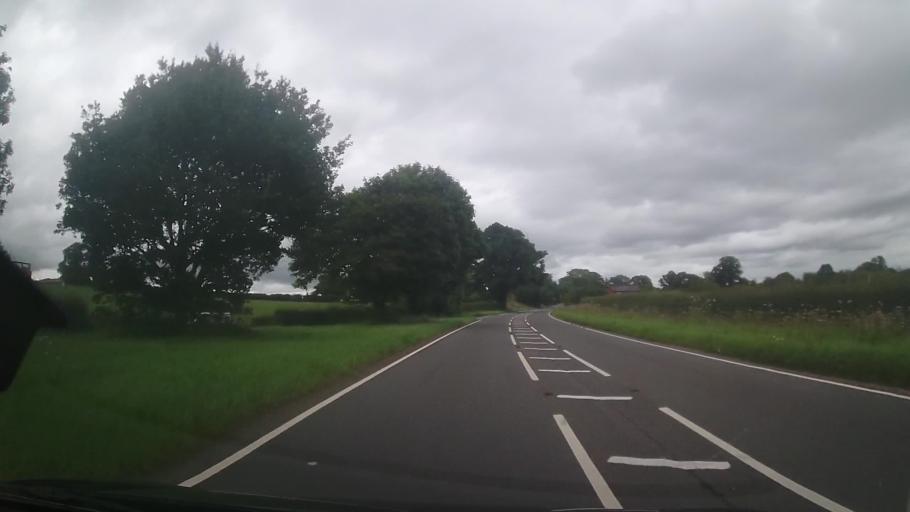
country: GB
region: England
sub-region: Shropshire
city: Ellesmere
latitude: 52.9164
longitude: -2.8328
